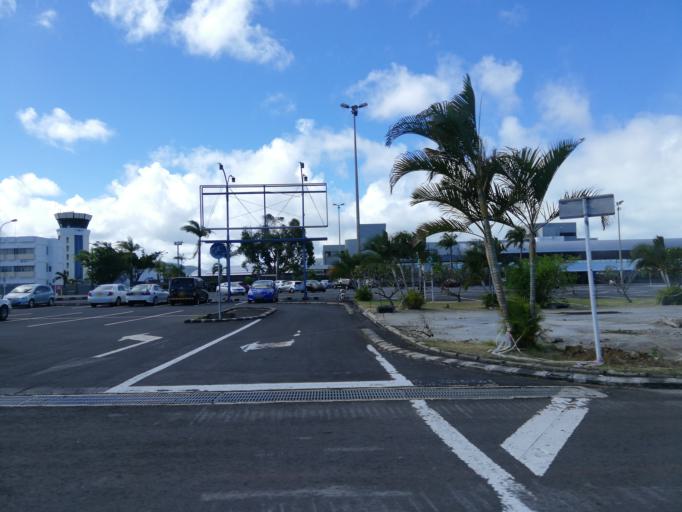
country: MU
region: Grand Port
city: Plaine Magnien
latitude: -20.4325
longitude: 57.6755
